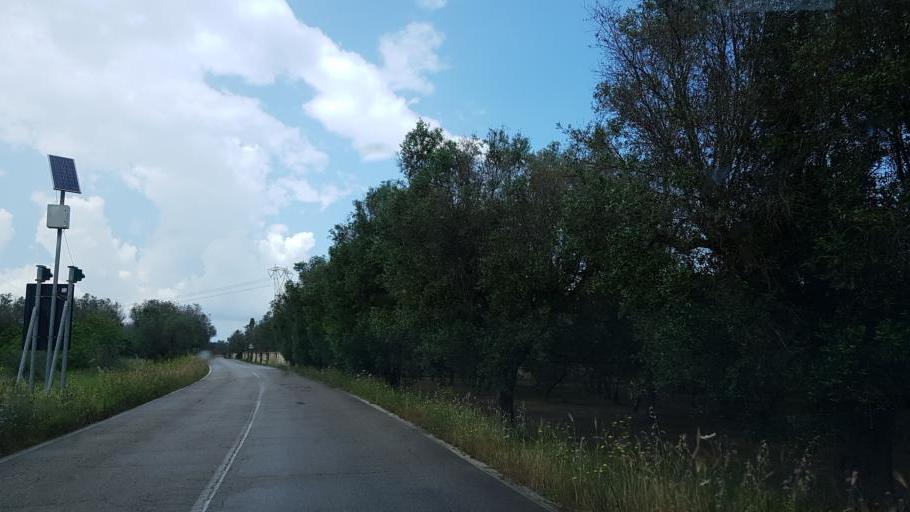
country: IT
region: Apulia
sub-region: Provincia di Brindisi
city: Cellino San Marco
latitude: 40.4756
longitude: 17.9379
